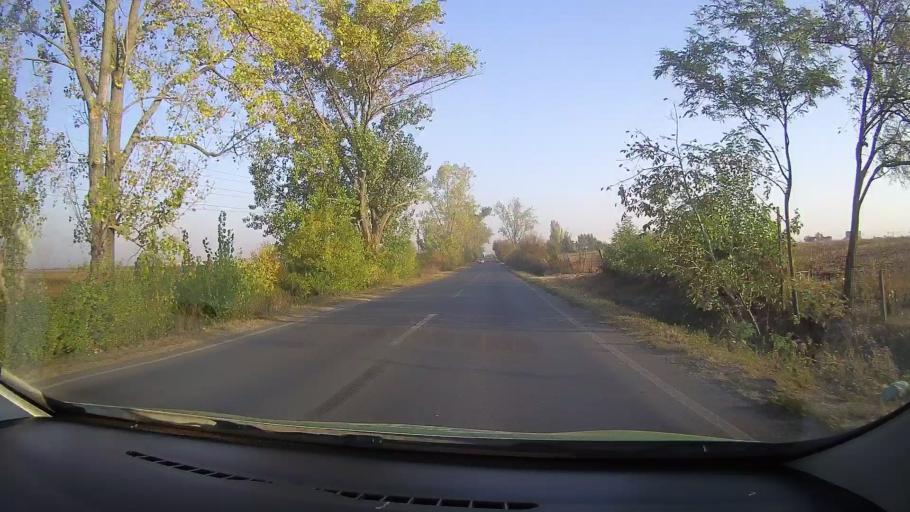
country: RO
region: Arad
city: Arad
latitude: 46.2233
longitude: 21.3205
